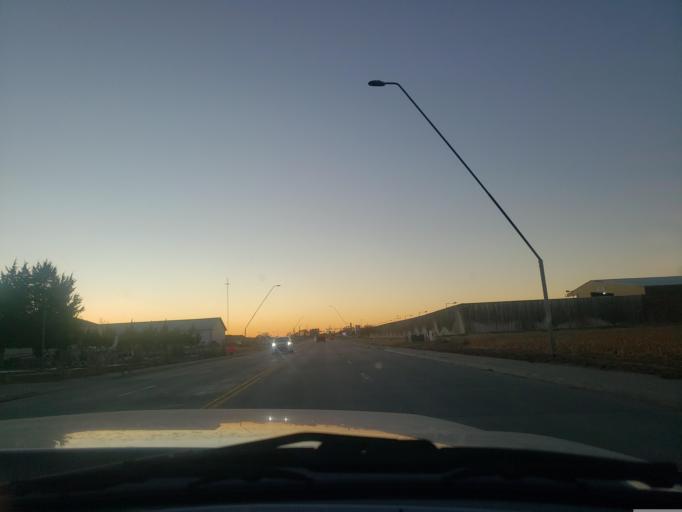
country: US
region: Kansas
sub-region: Finney County
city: Garden City
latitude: 37.9748
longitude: -100.8328
